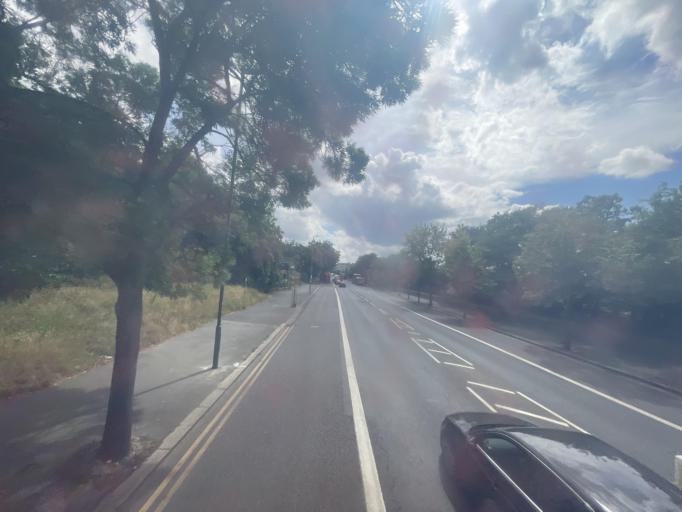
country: GB
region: England
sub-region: Greater London
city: Thornton Heath
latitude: 51.4226
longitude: -0.0769
